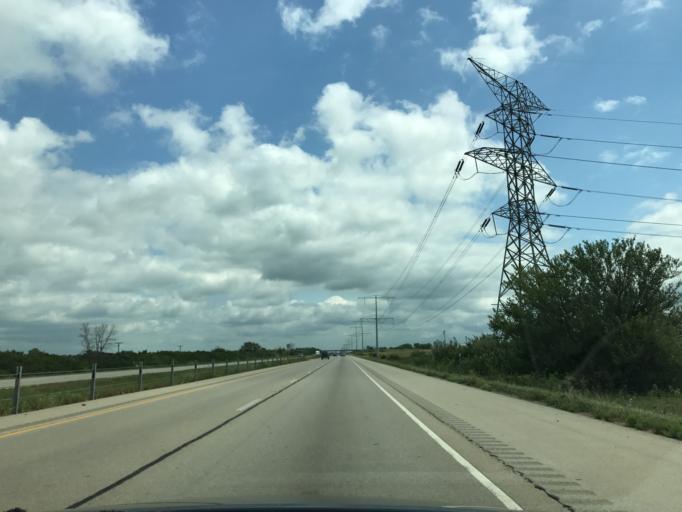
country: US
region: Illinois
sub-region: LaSalle County
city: Seneca
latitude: 41.3759
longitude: -88.6243
